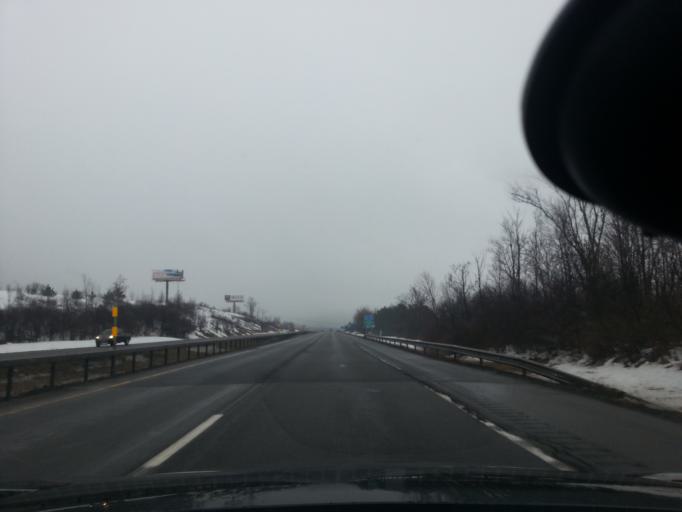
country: US
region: New York
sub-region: Jefferson County
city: Adams Center
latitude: 43.9214
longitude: -75.9738
